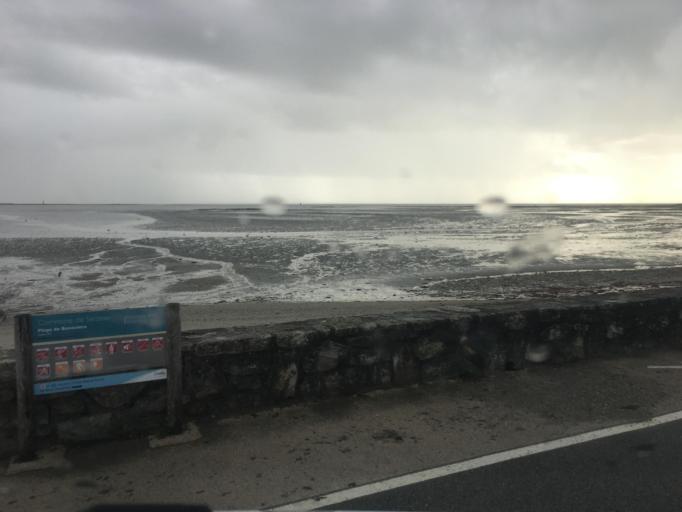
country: FR
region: Brittany
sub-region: Departement du Morbihan
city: Surzur
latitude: 47.5173
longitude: -2.6661
